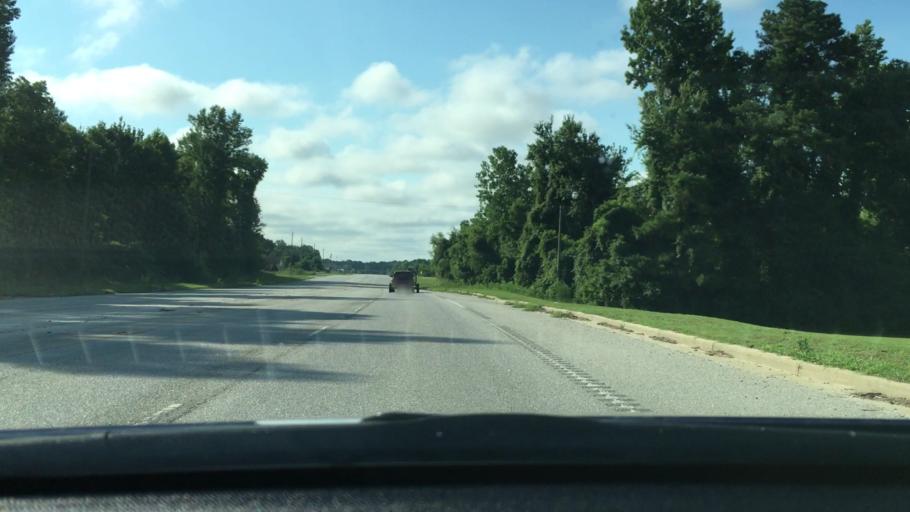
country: US
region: South Carolina
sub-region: Clarendon County
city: Manning
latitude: 33.7482
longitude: -80.2186
